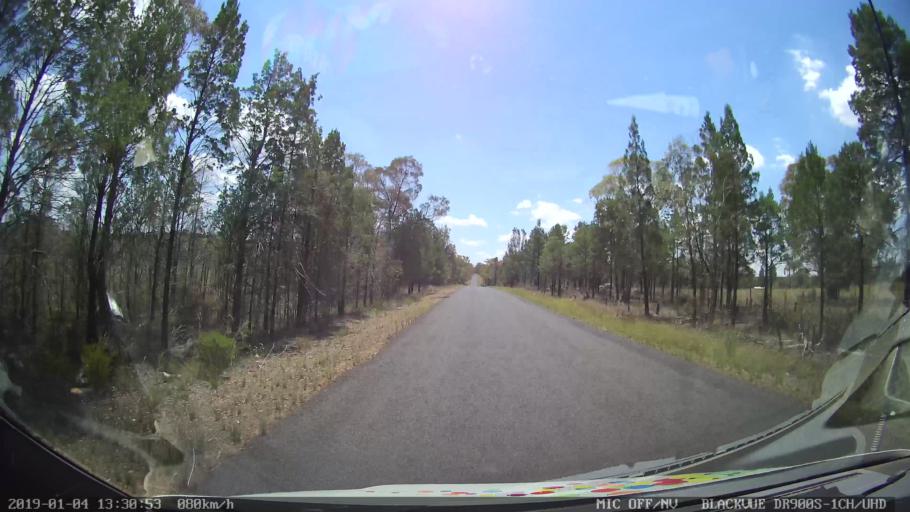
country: AU
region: New South Wales
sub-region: Parkes
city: Peak Hill
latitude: -32.6296
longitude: 148.5491
